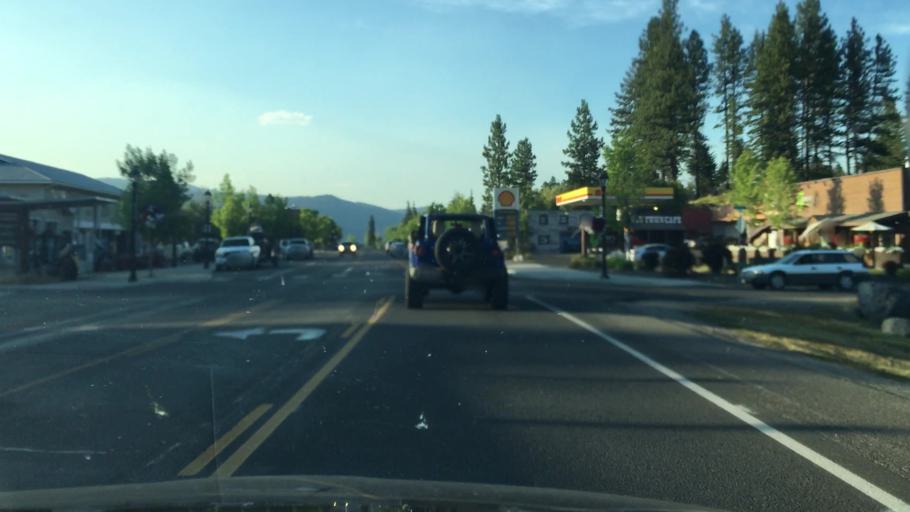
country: US
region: Idaho
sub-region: Valley County
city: McCall
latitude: 44.9057
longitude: -116.0975
